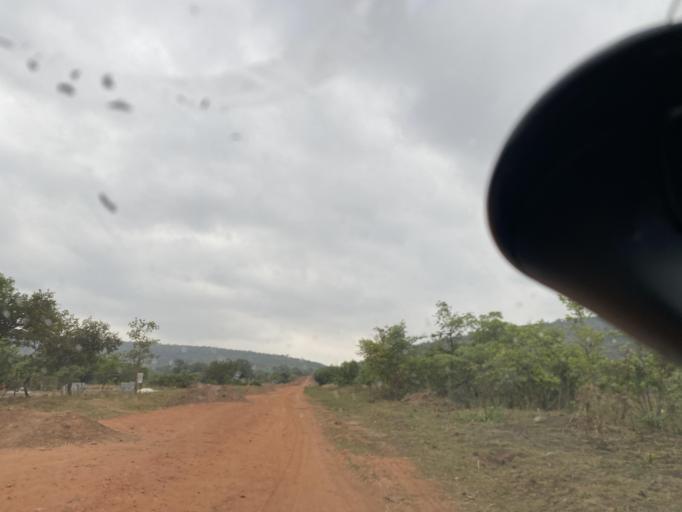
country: ZM
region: Lusaka
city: Chongwe
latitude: -15.1876
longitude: 28.7635
